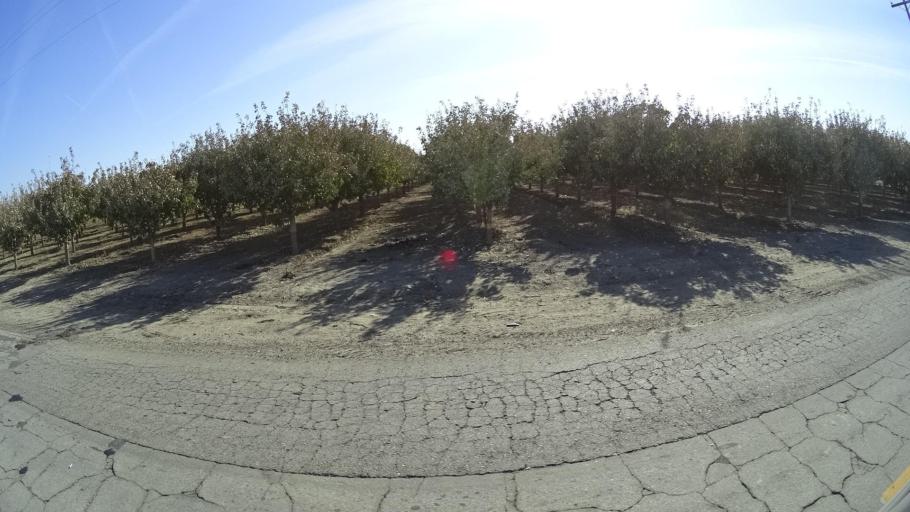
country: US
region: California
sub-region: Kern County
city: Wasco
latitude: 35.7031
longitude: -119.4000
